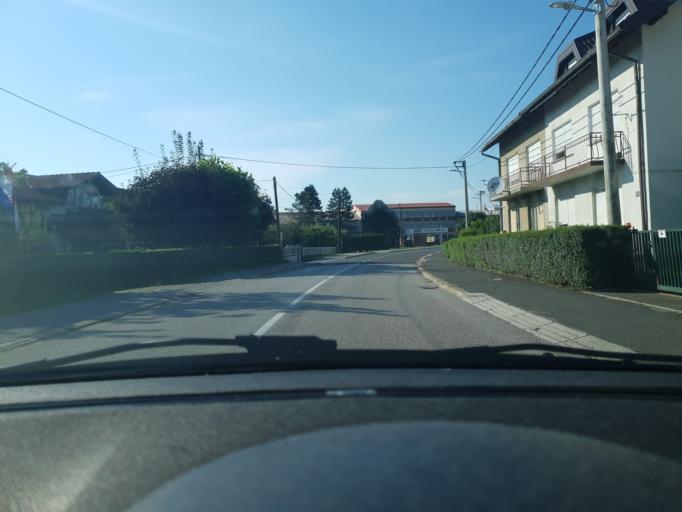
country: HR
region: Krapinsko-Zagorska
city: Oroslavje
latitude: 45.9927
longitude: 15.9170
